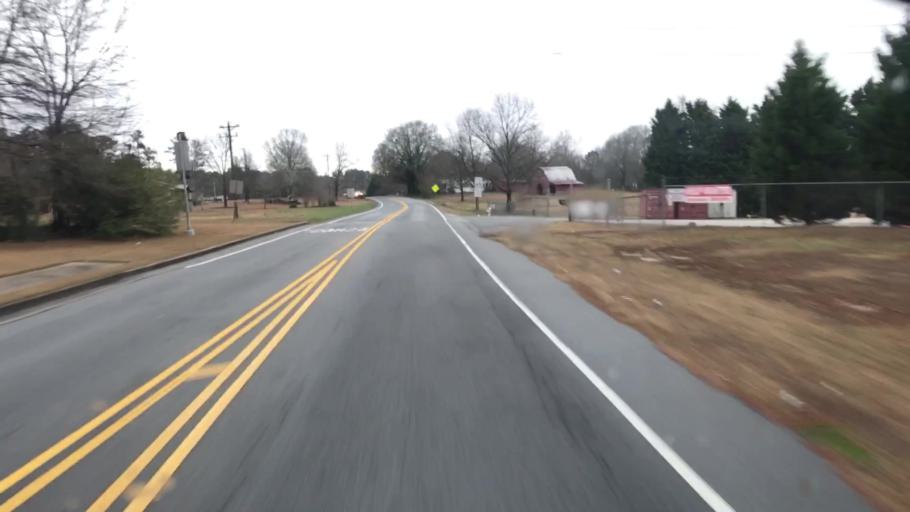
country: US
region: Georgia
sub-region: Walton County
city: Loganville
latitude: 33.8180
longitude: -83.9629
